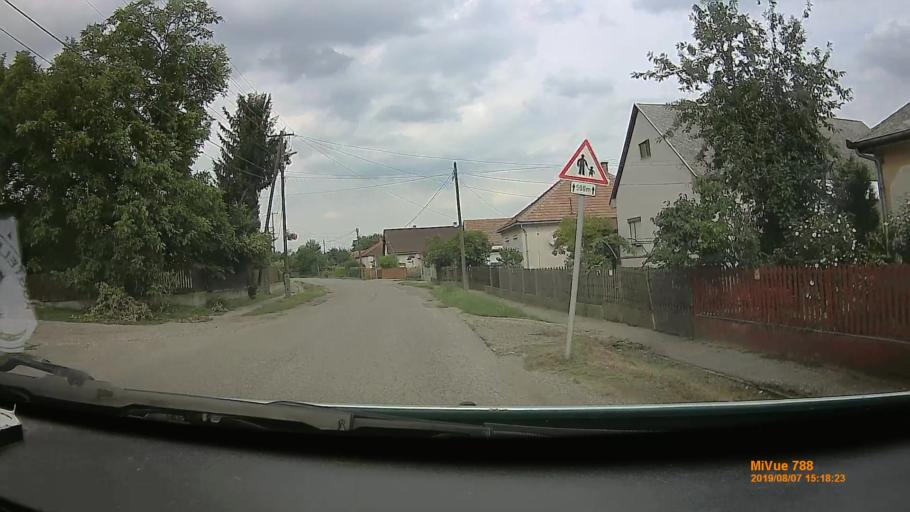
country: HU
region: Borsod-Abauj-Zemplen
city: Encs
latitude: 48.3443
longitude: 21.1387
